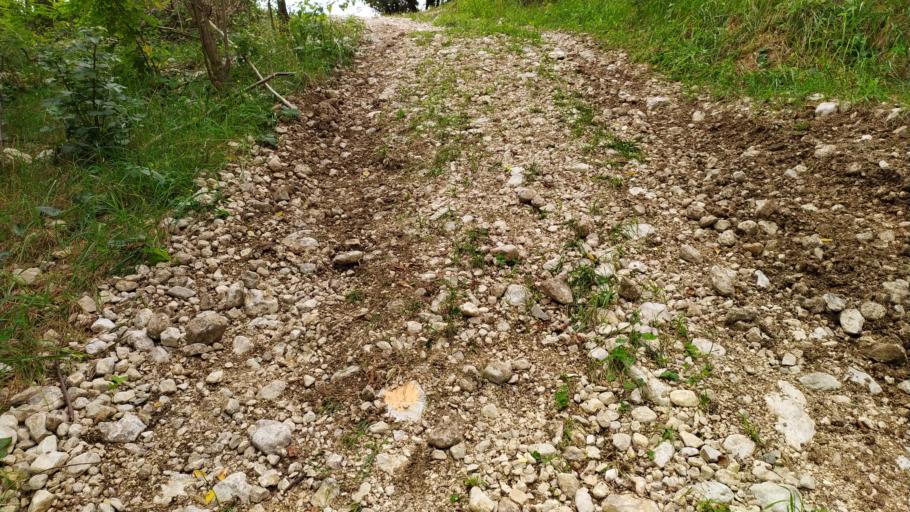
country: IT
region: Friuli Venezia Giulia
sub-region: Provincia di Pordenone
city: Aviano-Castello
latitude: 46.0830
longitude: 12.5756
